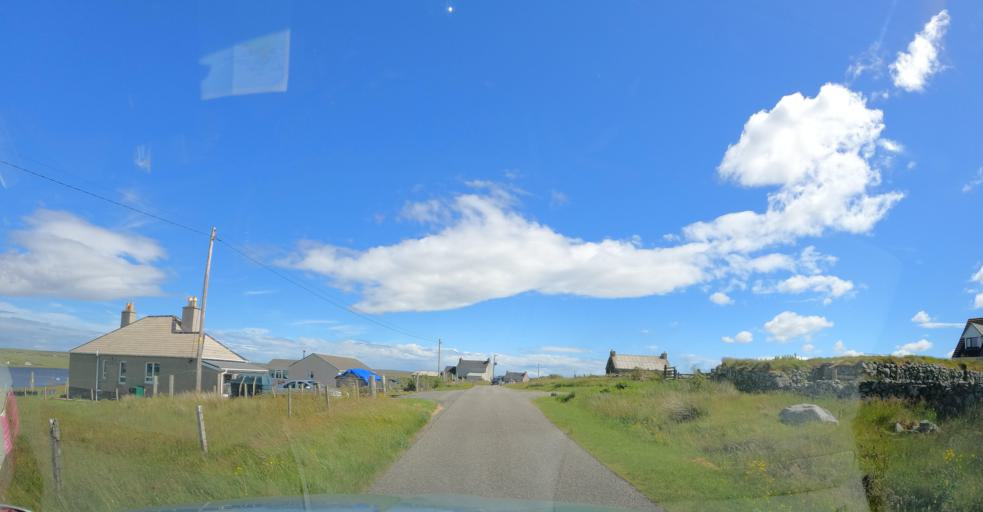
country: GB
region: Scotland
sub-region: Eilean Siar
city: Isle of Lewis
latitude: 58.3550
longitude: -6.5501
